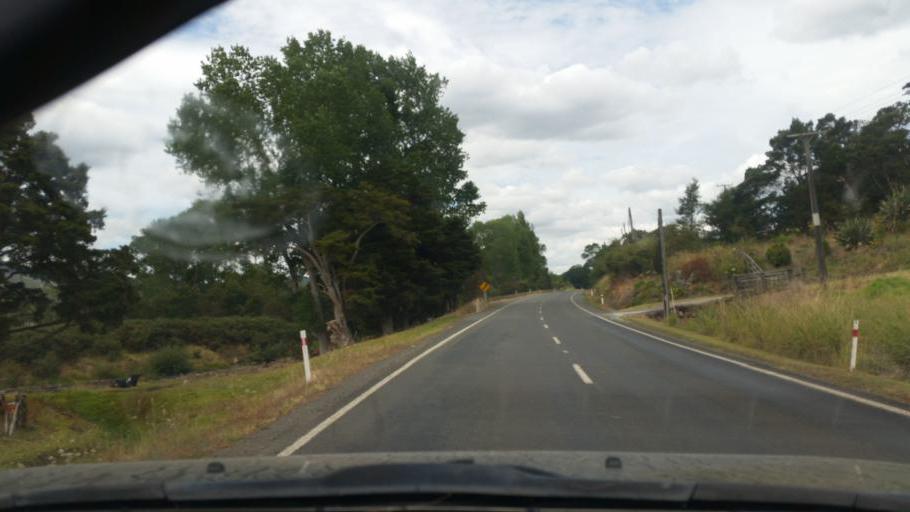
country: NZ
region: Northland
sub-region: Kaipara District
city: Dargaville
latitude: -35.7705
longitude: 173.6979
